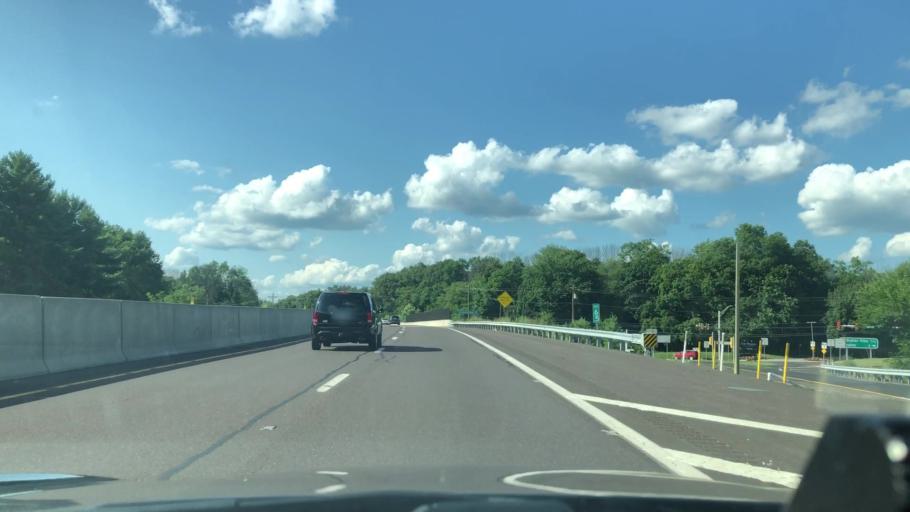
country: US
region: Pennsylvania
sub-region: Montgomery County
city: Fort Washington
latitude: 40.1604
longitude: -75.2012
